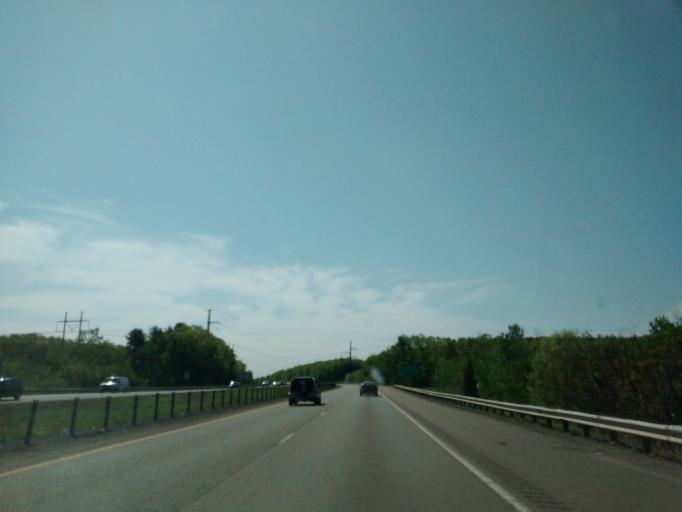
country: US
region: Massachusetts
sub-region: Worcester County
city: Sutton
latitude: 42.1433
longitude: -71.7164
